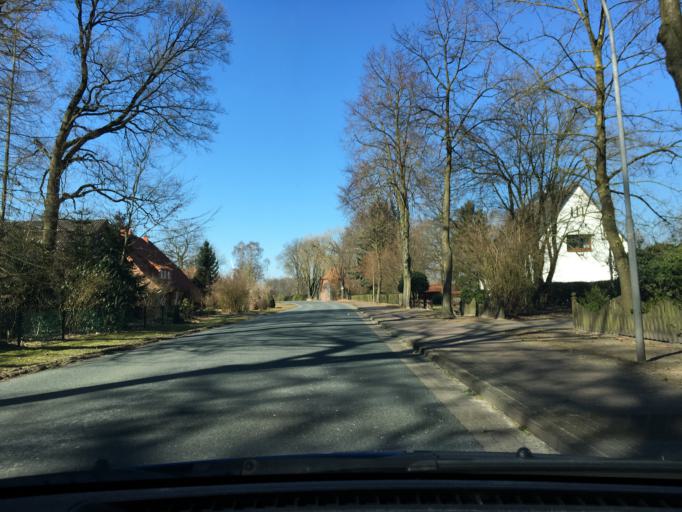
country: DE
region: Lower Saxony
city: Hemslingen
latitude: 53.0699
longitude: 9.6470
